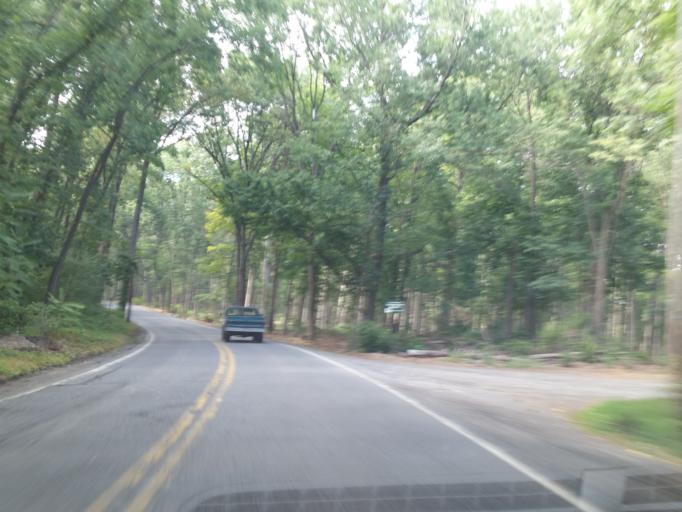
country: US
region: Pennsylvania
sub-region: Lebanon County
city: Campbelltown
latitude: 40.2293
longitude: -76.5043
